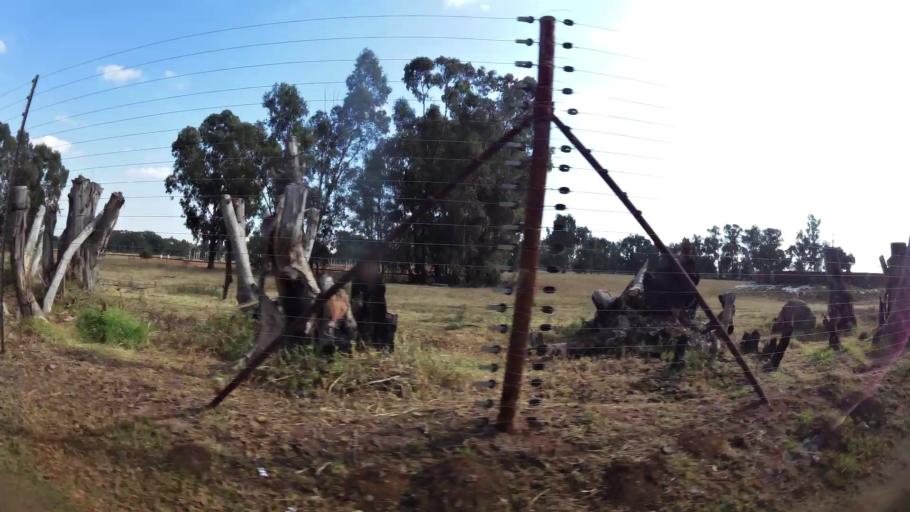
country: ZA
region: Gauteng
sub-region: Ekurhuleni Metropolitan Municipality
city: Benoni
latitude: -26.0902
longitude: 28.3640
